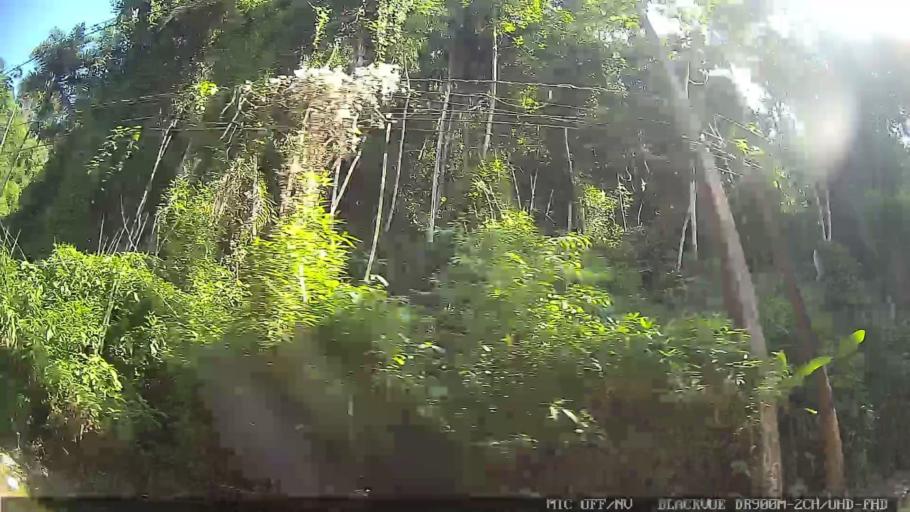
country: BR
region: Sao Paulo
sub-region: Santos
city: Santos
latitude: -24.0004
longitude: -46.3119
